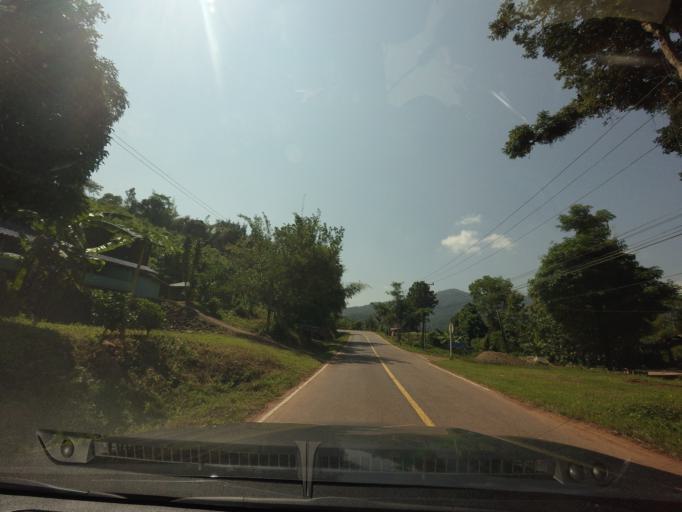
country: TH
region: Nan
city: Bo Kluea
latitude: 19.0731
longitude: 101.1589
